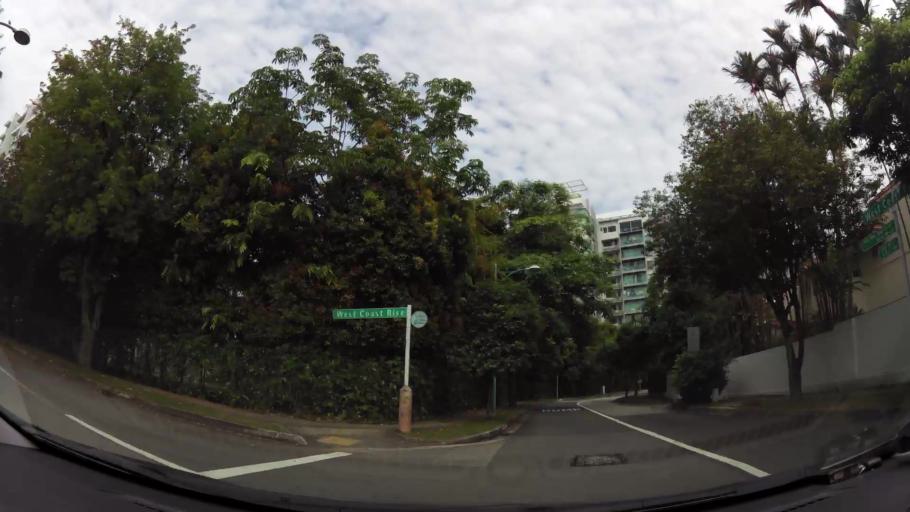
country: SG
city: Singapore
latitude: 1.3171
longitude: 103.7546
